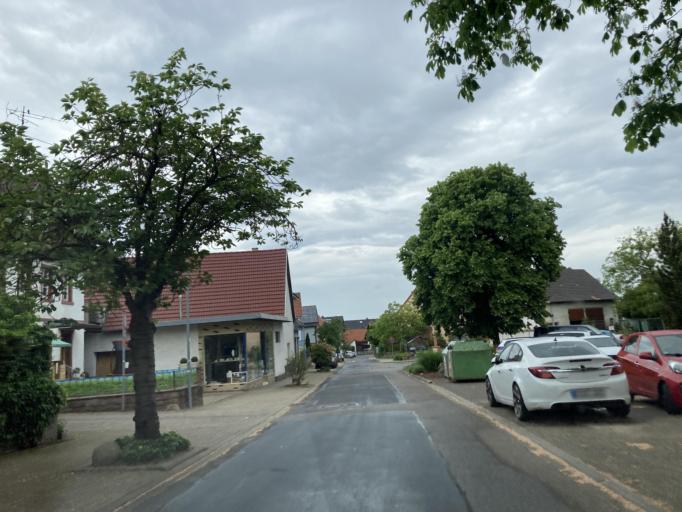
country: DE
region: Baden-Wuerttemberg
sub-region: Karlsruhe Region
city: Malsch
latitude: 48.8817
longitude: 8.3368
